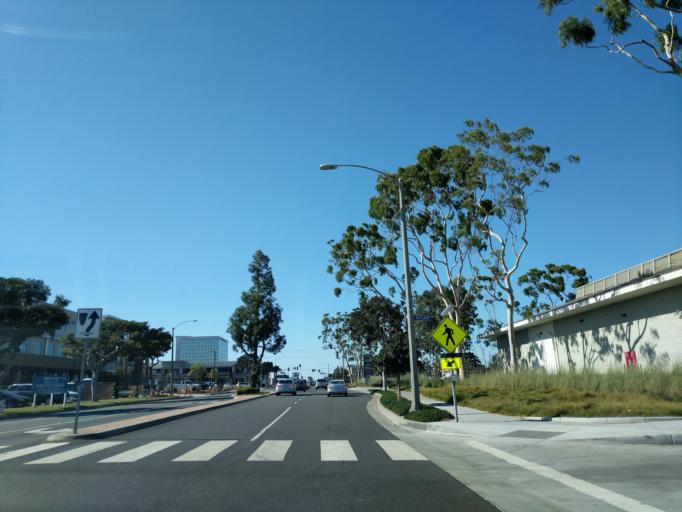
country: US
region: California
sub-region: Orange County
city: Costa Mesa
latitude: 33.6272
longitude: -117.9067
